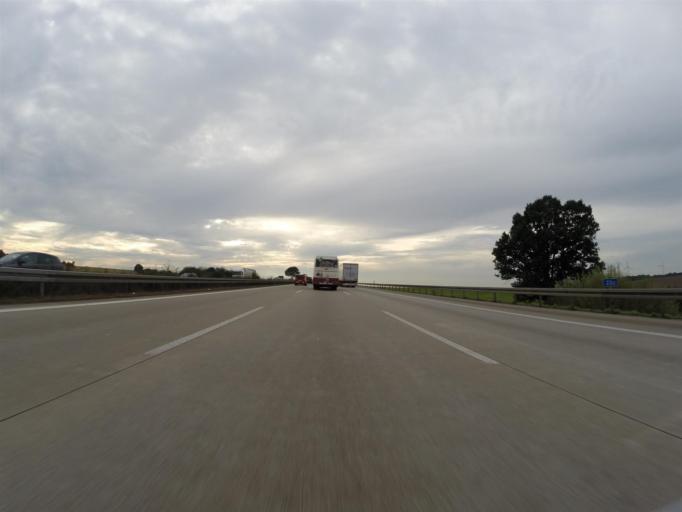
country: DE
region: Saxony
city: Wilsdruff
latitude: 51.0599
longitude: 13.4678
